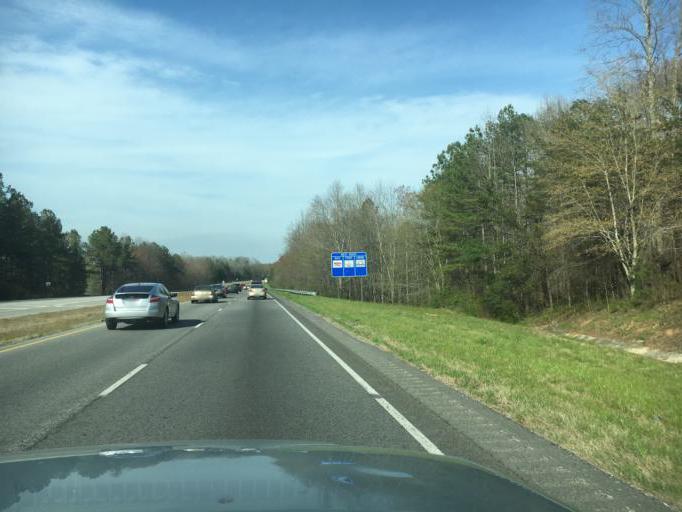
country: US
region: Georgia
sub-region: Habersham County
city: Baldwin
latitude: 34.5034
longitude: -83.5697
